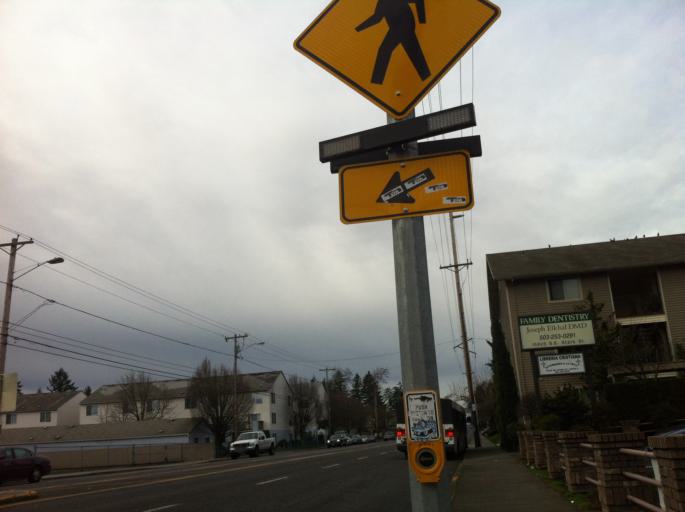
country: US
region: Oregon
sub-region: Multnomah County
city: Fairview
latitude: 45.5193
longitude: -122.4992
